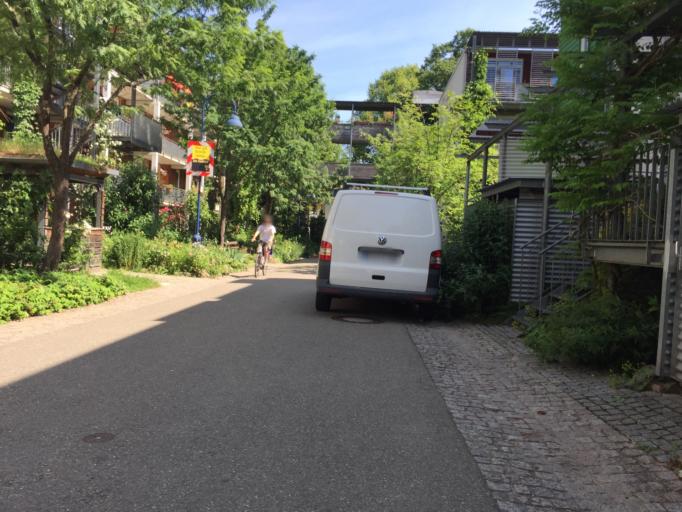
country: DE
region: Baden-Wuerttemberg
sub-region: Freiburg Region
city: Merzhausen
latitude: 47.9753
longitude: 7.8242
